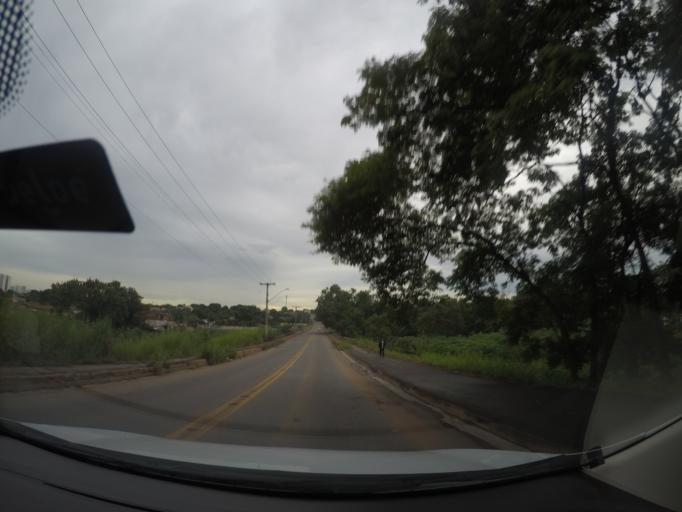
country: BR
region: Goias
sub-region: Goiania
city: Goiania
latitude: -16.6527
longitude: -49.2987
